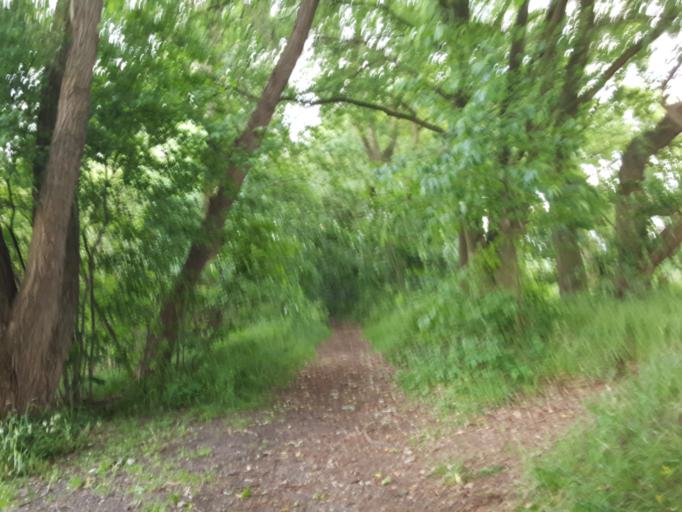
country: DE
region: Schleswig-Holstein
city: Oststeinbek
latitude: 53.5128
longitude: 10.1356
